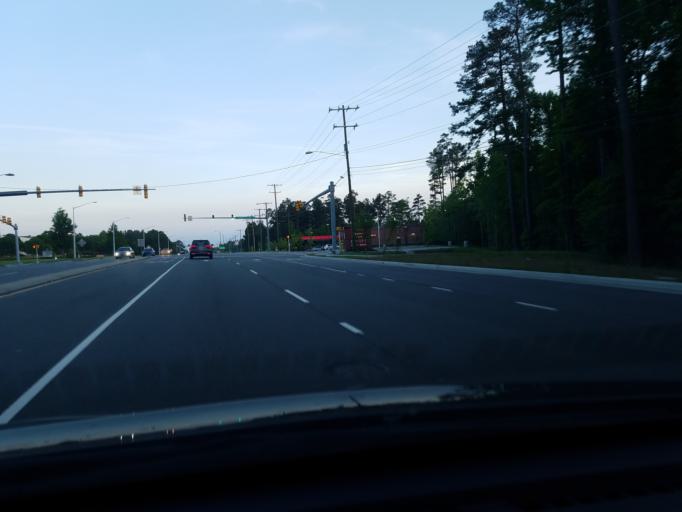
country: US
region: North Carolina
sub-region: Orange County
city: Chapel Hill
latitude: 35.9090
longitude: -78.9606
